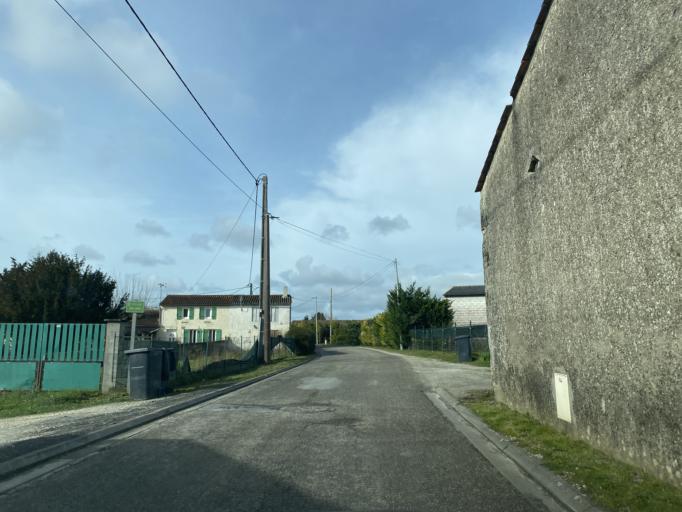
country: FR
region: Aquitaine
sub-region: Departement de la Gironde
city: Moulis-en-Medoc
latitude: 45.0548
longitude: -0.7666
